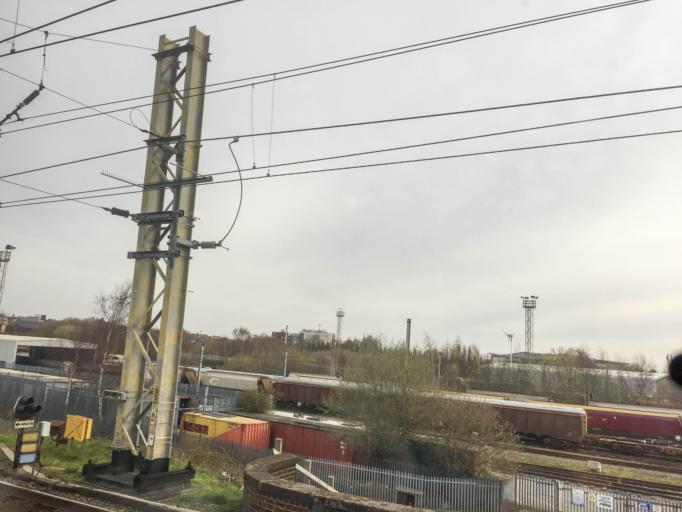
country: GB
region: England
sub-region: Warrington
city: Warrington
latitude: 53.3829
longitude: -2.6025
